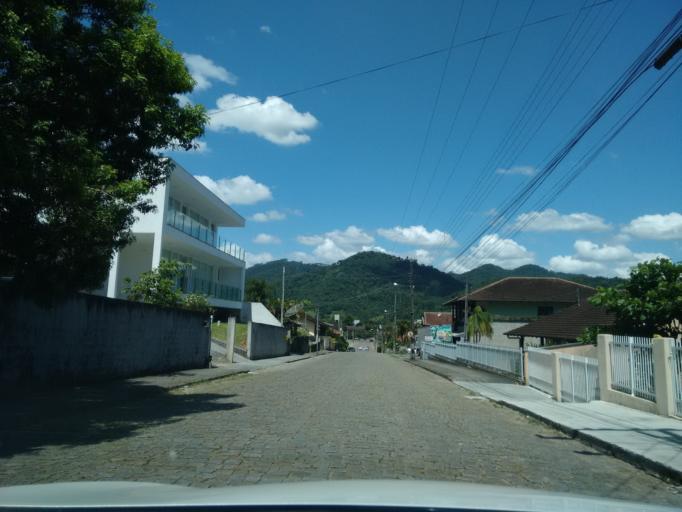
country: BR
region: Santa Catarina
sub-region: Pomerode
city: Pomerode
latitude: -26.7505
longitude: -49.1767
